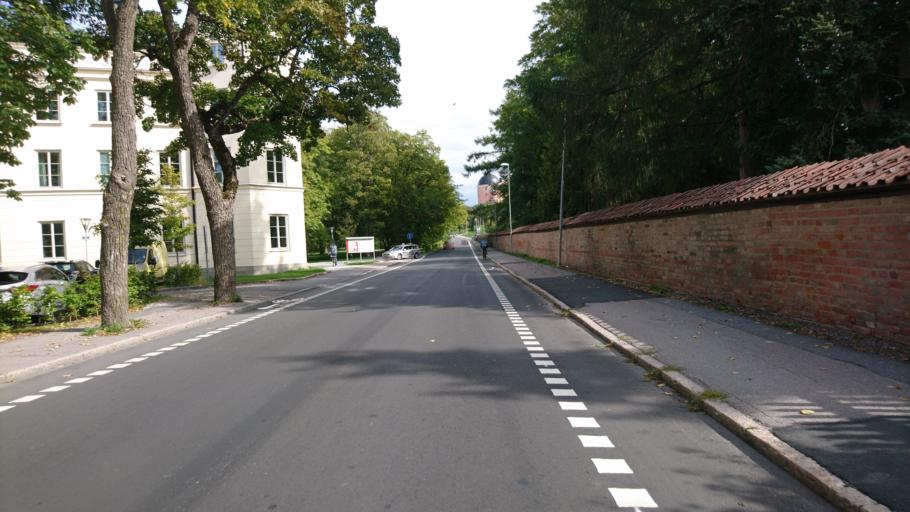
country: SE
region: Uppsala
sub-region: Uppsala Kommun
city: Uppsala
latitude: 59.8531
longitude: 17.6281
